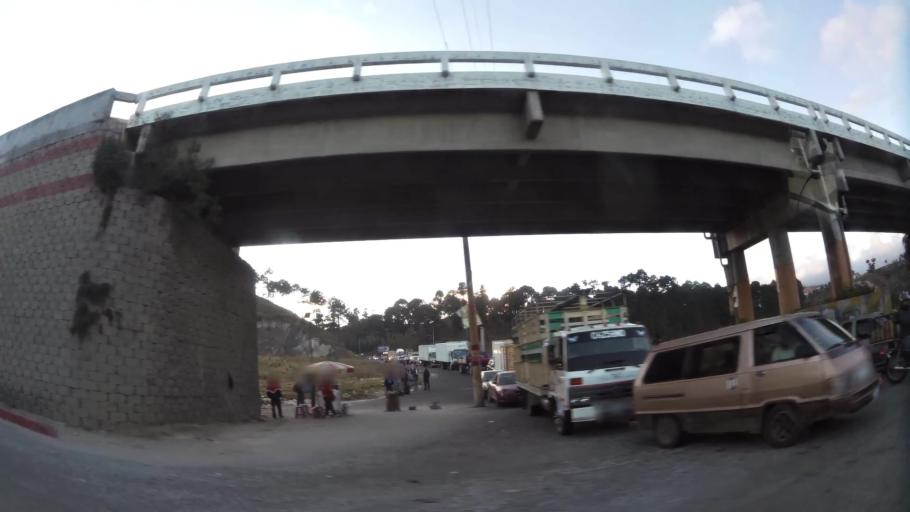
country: GT
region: Quetzaltenango
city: Salcaja
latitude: 14.8647
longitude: -91.4687
